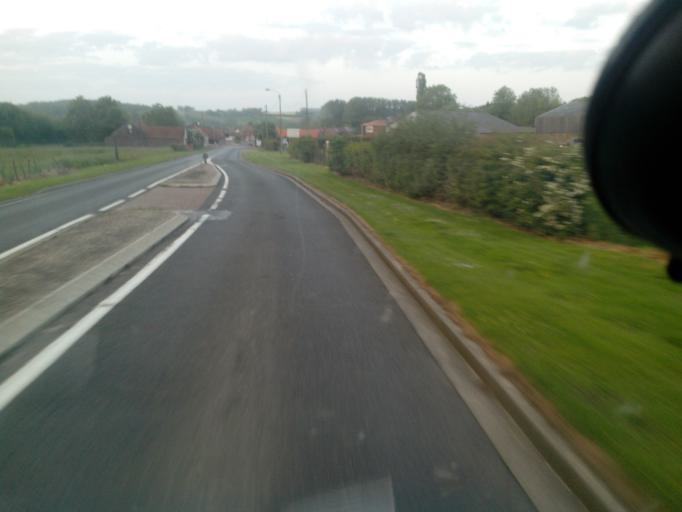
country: FR
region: Picardie
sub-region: Departement de la Somme
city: Crecy-en-Ponthieu
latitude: 50.2671
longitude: 1.9812
